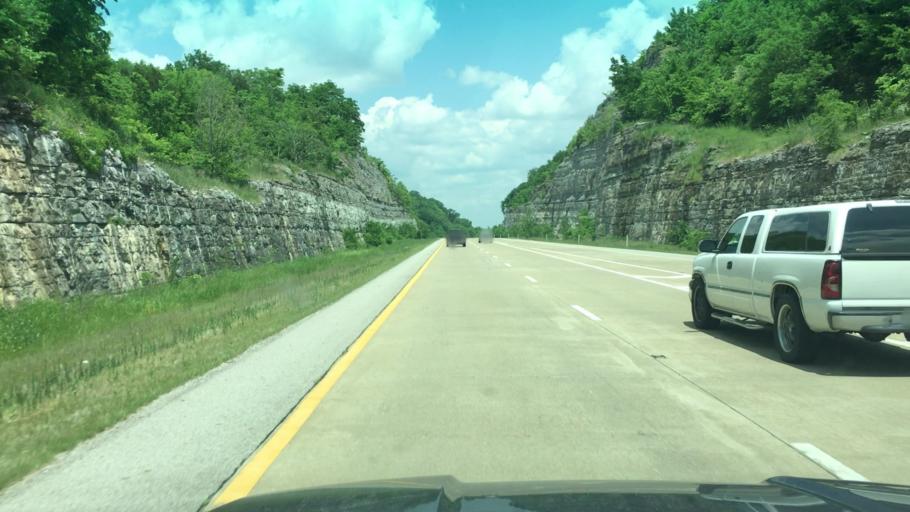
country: US
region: Tennessee
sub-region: Williamson County
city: Thompson's Station
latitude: 35.8254
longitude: -86.8336
